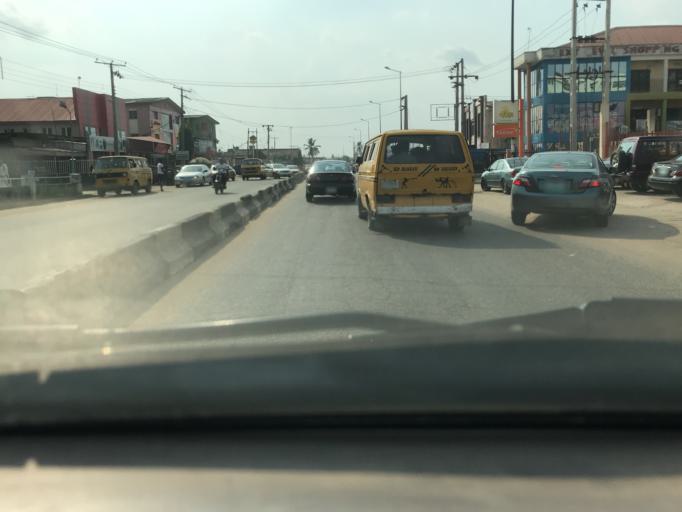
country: NG
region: Lagos
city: Agege
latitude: 6.6023
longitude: 3.3062
